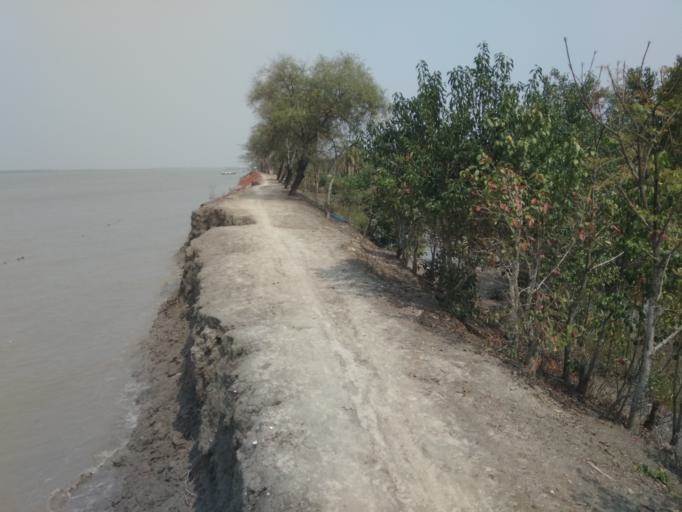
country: IN
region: West Bengal
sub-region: North 24 Parganas
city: Gosaba
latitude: 22.2499
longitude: 89.2501
